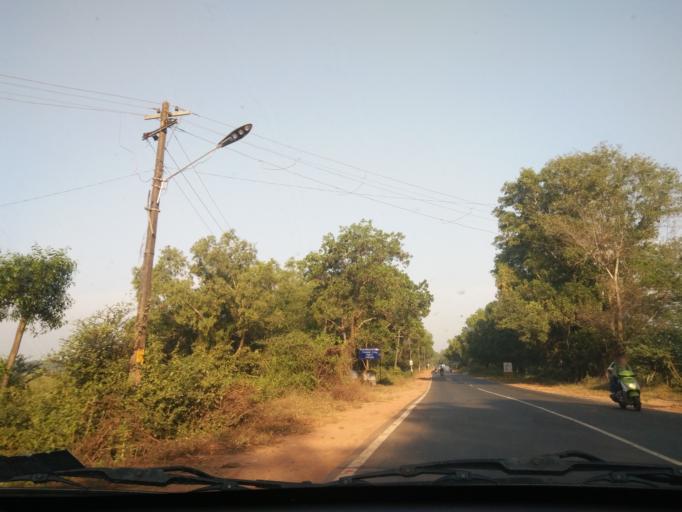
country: IN
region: Goa
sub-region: South Goa
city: Chinchinim
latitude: 15.2094
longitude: 73.9907
